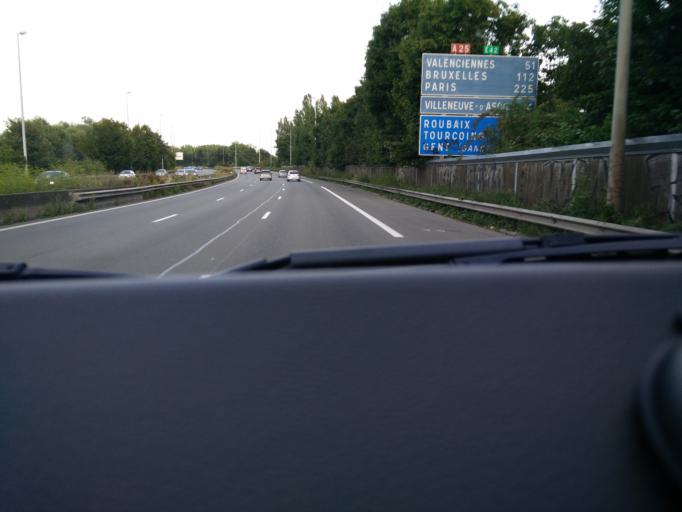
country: FR
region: Nord-Pas-de-Calais
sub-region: Departement du Nord
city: Sequedin
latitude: 50.6169
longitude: 2.9818
